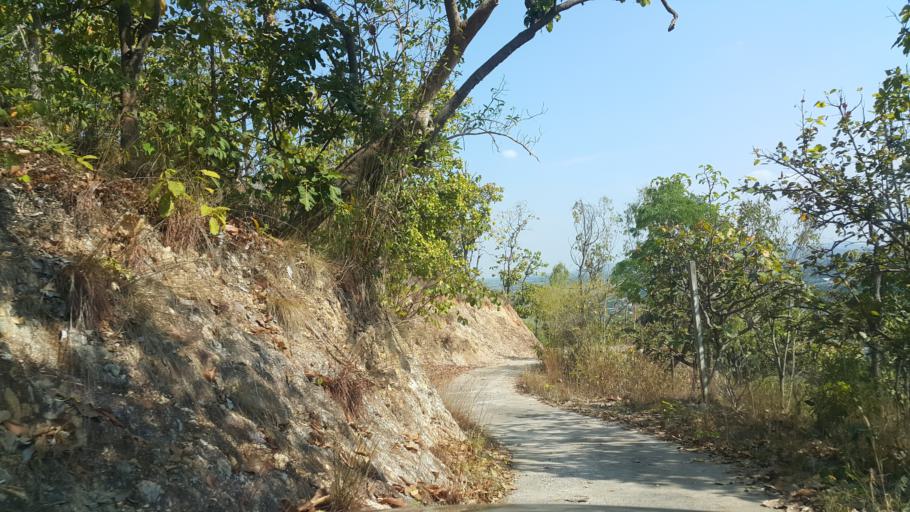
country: TH
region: Sukhothai
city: Thung Saliam
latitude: 17.3401
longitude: 99.5917
